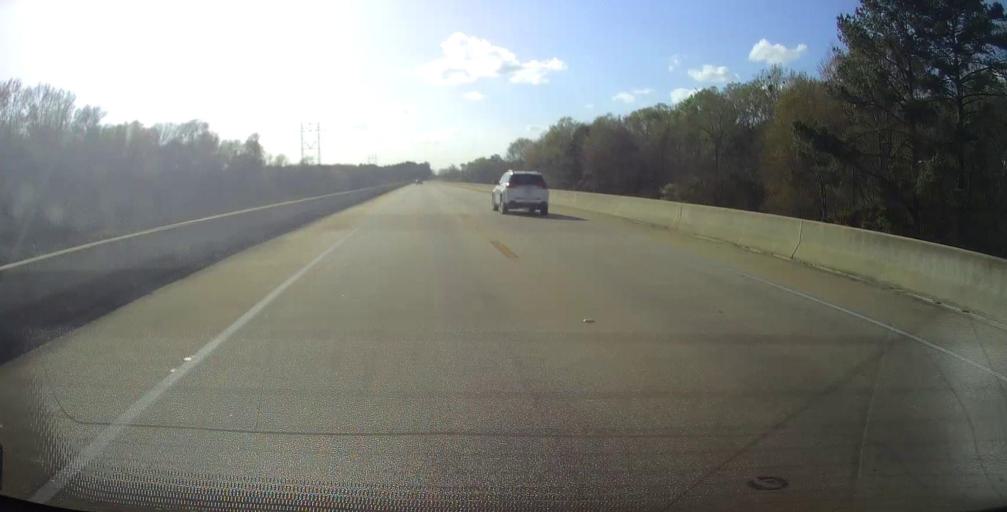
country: US
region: Georgia
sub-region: Montgomery County
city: Mount Vernon
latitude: 32.1912
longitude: -82.6259
